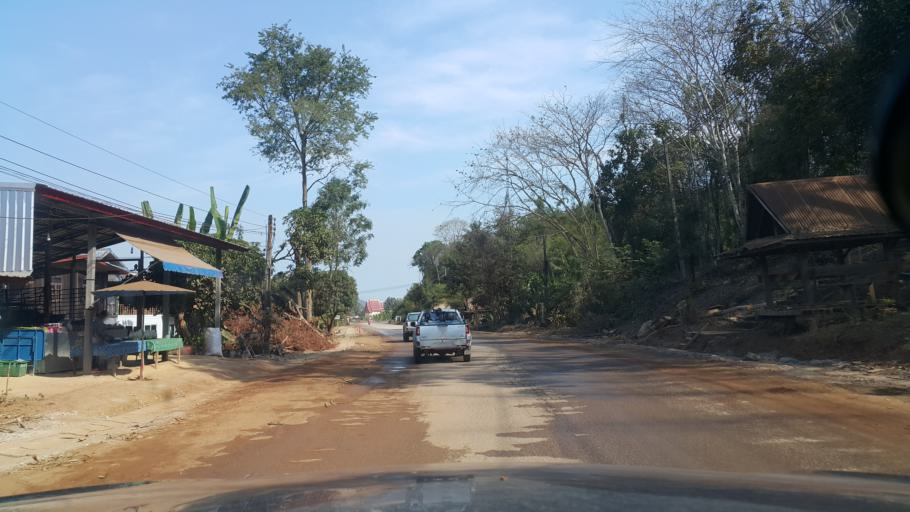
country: TH
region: Loei
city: Pak Chom
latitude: 18.0805
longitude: 101.9472
